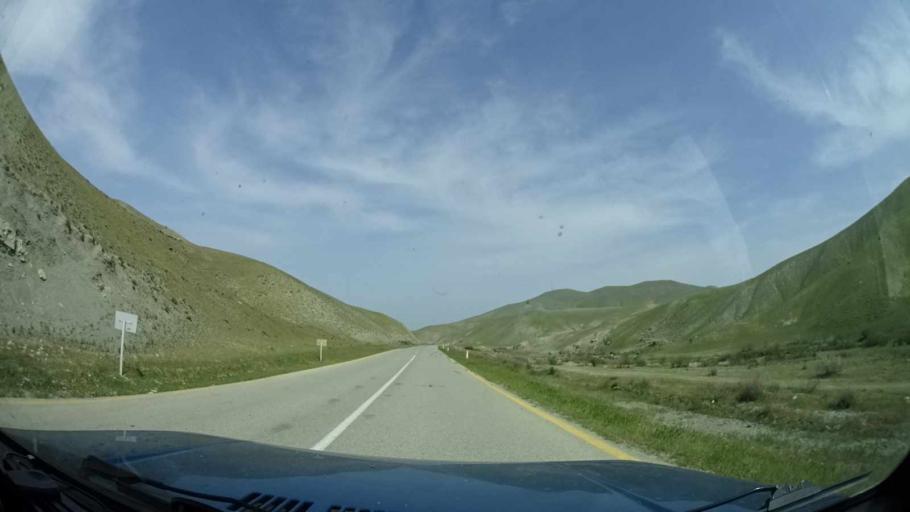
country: AZ
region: Xizi
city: Kilyazi
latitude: 40.8492
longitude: 49.2593
